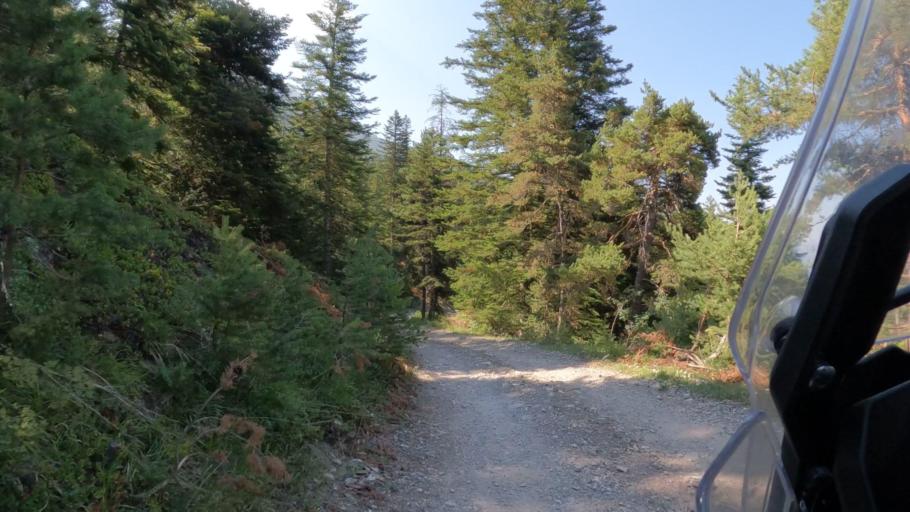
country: FR
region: Provence-Alpes-Cote d'Azur
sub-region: Departement des Hautes-Alpes
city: Embrun
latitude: 44.5962
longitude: 6.5629
